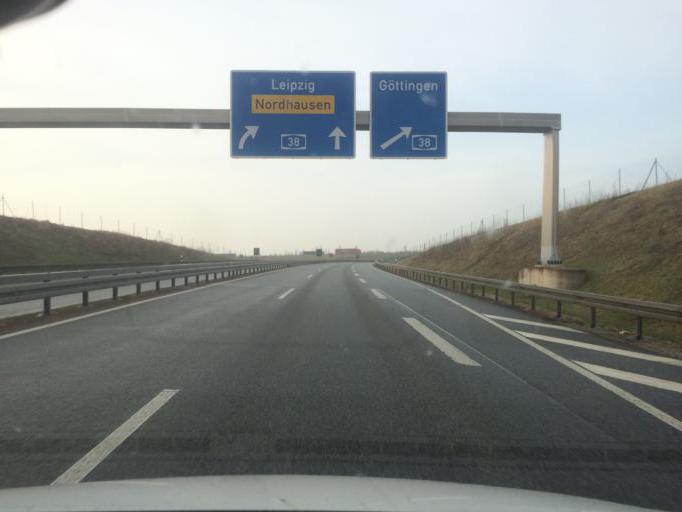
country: DE
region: Thuringia
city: Nohra
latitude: 51.4932
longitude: 10.7181
